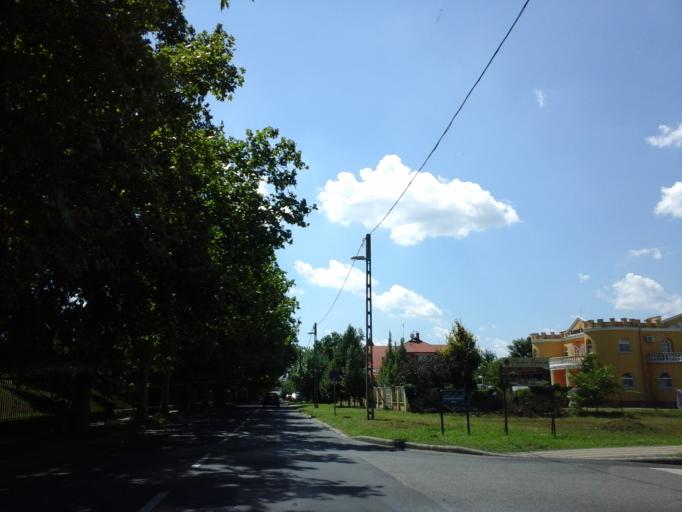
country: HU
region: Hajdu-Bihar
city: Hajduszoboszlo
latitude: 47.4542
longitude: 21.4033
